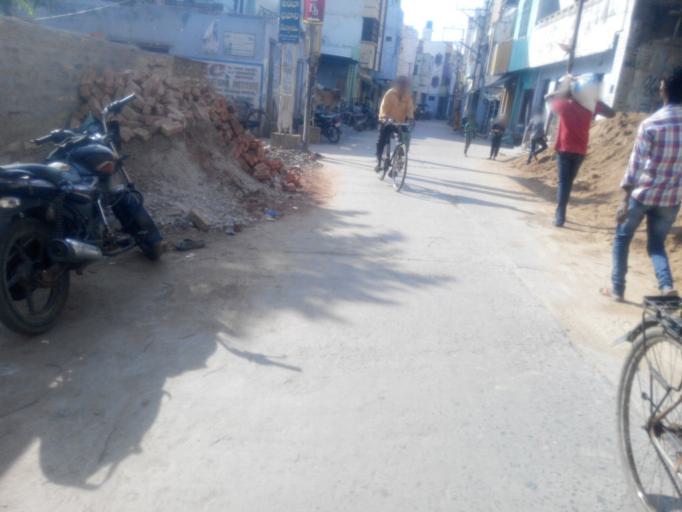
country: IN
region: Andhra Pradesh
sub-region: Kurnool
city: Nandyal
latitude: 15.4907
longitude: 78.4836
